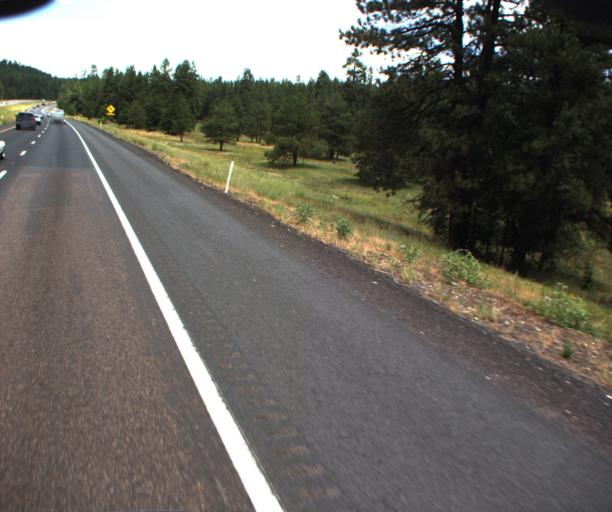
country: US
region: Arizona
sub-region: Coconino County
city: Mountainaire
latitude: 34.9667
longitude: -111.6819
